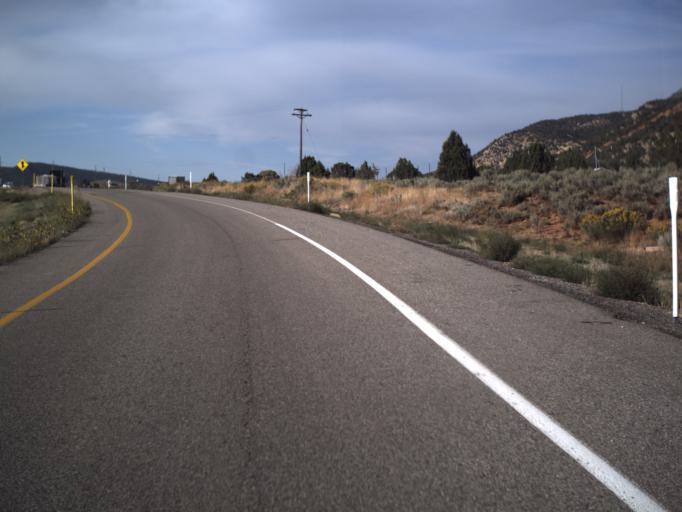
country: US
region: Utah
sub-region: Washington County
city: Toquerville
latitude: 37.4554
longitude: -113.2273
